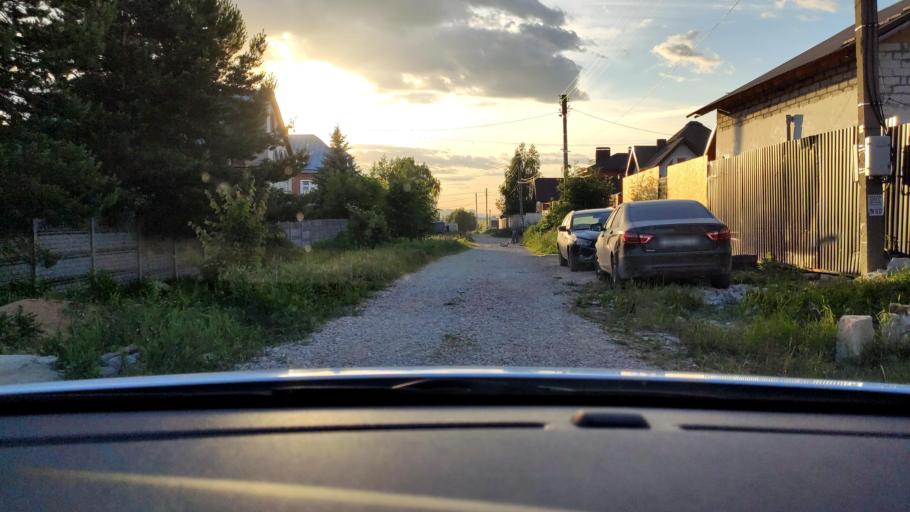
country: RU
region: Tatarstan
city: Stolbishchi
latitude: 55.7572
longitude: 49.2824
